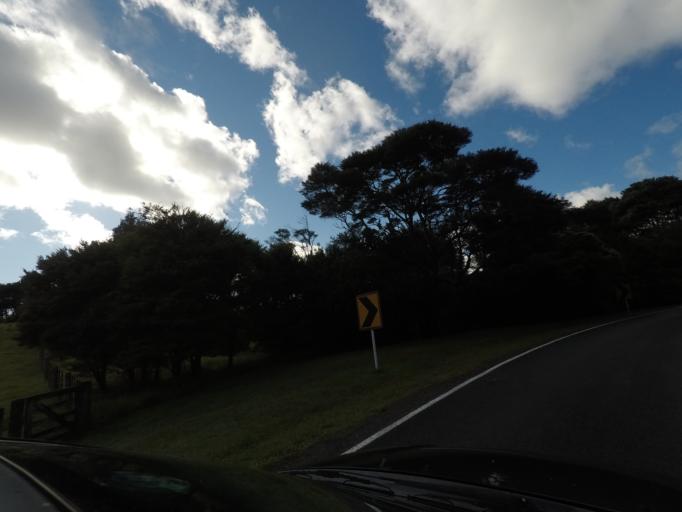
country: NZ
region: Auckland
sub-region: Auckland
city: Titirangi
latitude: -37.0062
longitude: 174.5630
